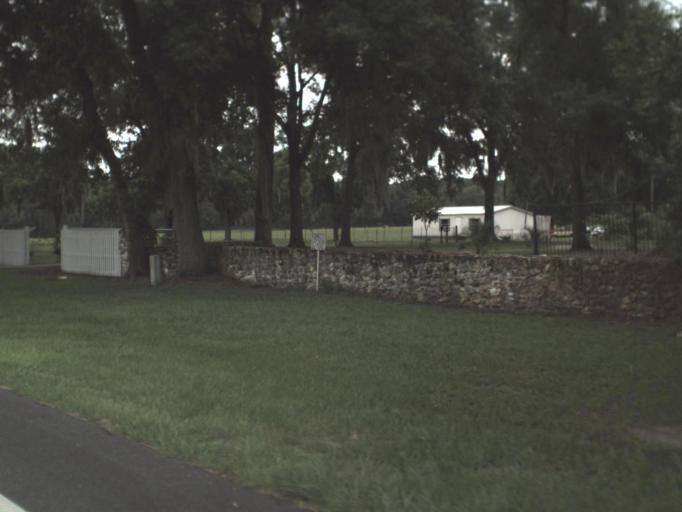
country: US
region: Florida
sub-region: Levy County
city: Williston
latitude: 29.3606
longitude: -82.4558
